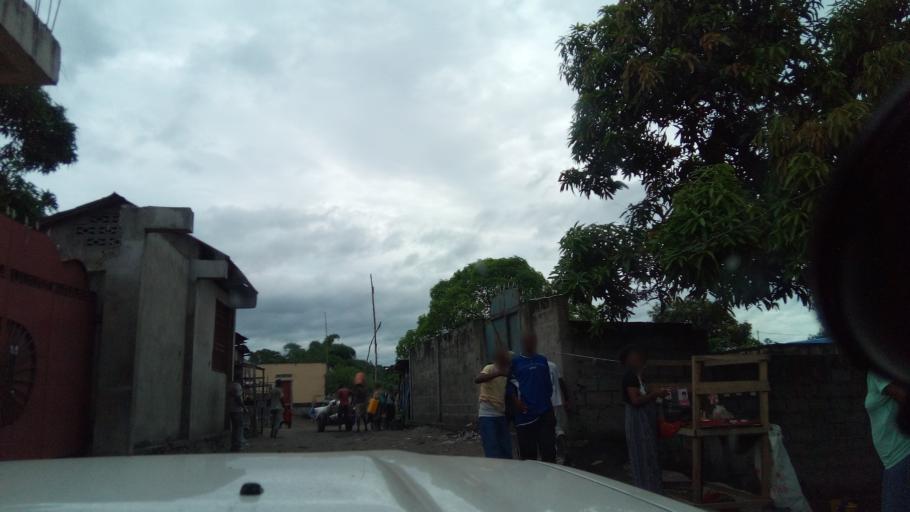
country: CD
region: Kinshasa
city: Masina
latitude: -4.3190
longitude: 15.5134
